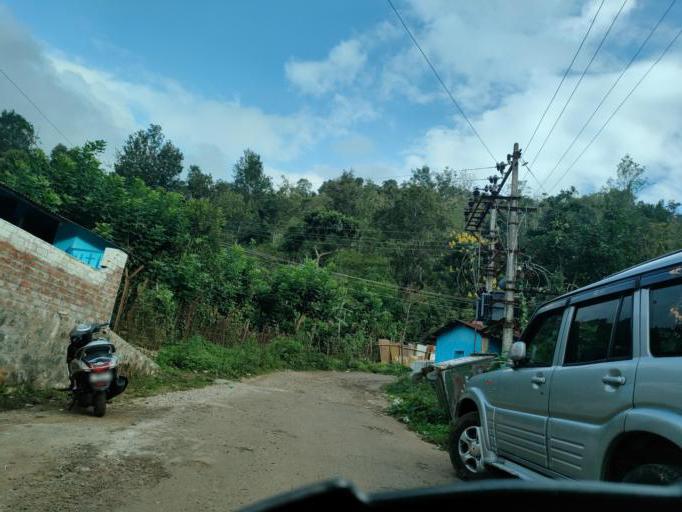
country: IN
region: Tamil Nadu
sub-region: Dindigul
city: Kodaikanal
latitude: 10.2830
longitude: 77.5305
